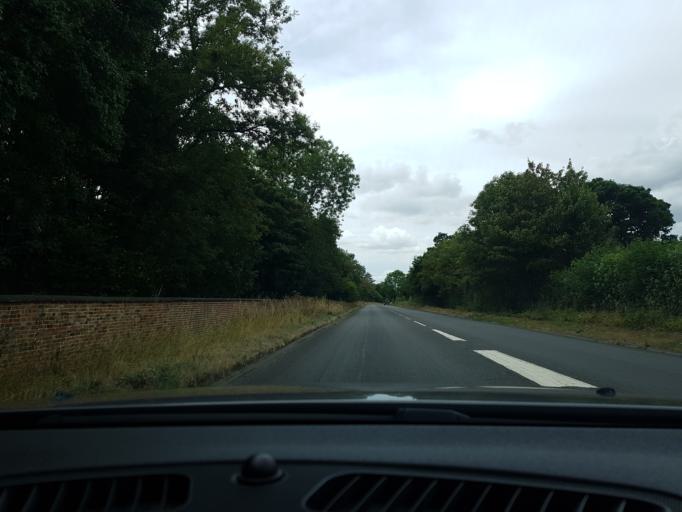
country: GB
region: England
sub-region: West Berkshire
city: Newbury
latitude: 51.4088
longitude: -1.3632
